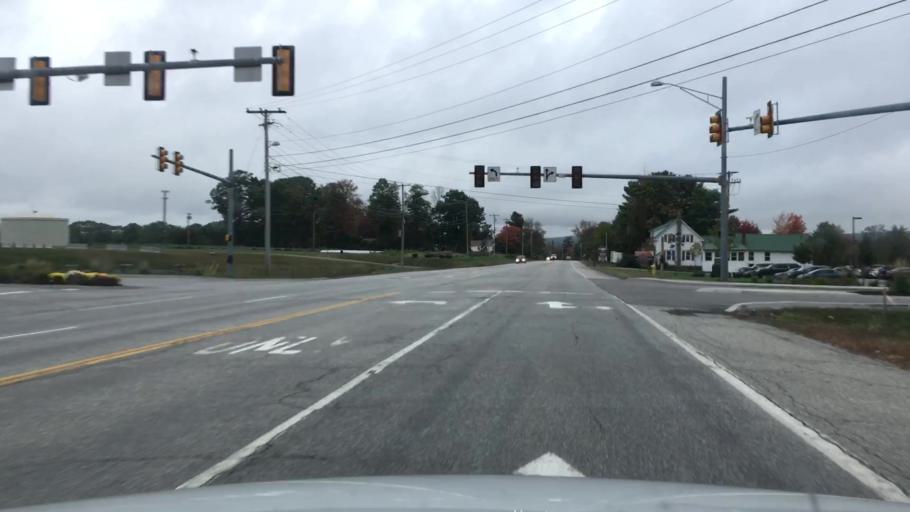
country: US
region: Maine
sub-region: Androscoggin County
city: Mechanic Falls
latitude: 44.1163
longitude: -70.4433
